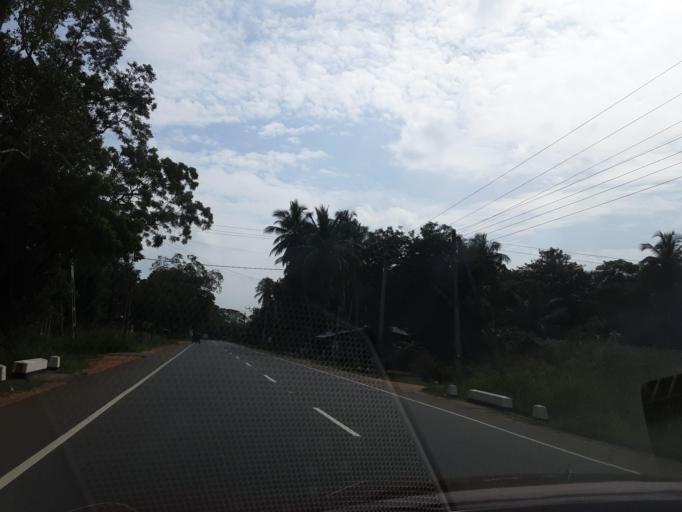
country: LK
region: North Central
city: Anuradhapura
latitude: 8.5208
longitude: 80.5016
